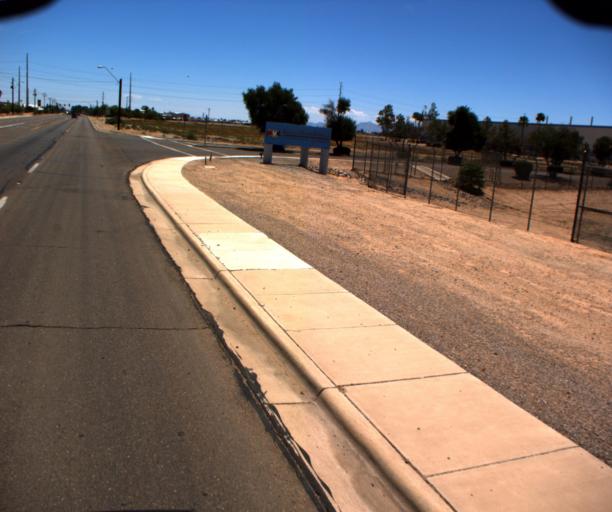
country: US
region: Arizona
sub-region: Pinal County
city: Casa Grande
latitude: 32.8794
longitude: -111.7792
